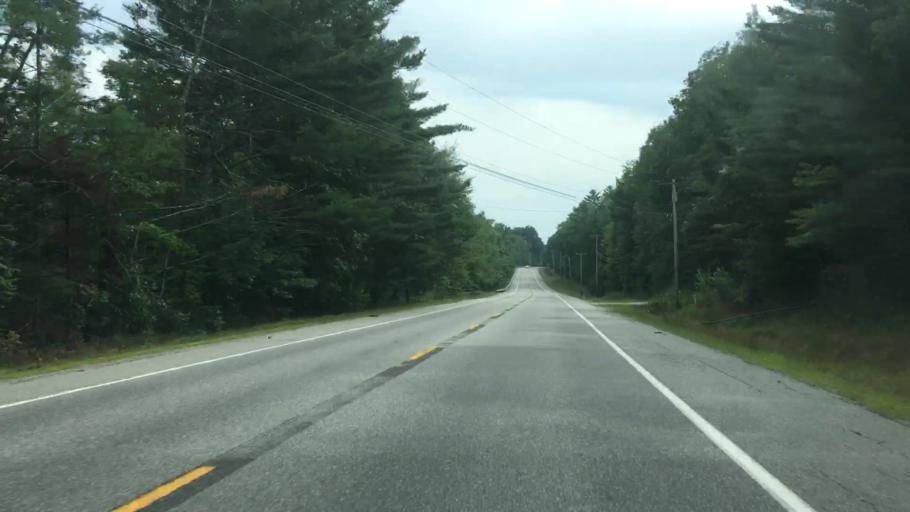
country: US
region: Maine
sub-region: Oxford County
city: Bethel
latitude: 44.4743
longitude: -70.7974
